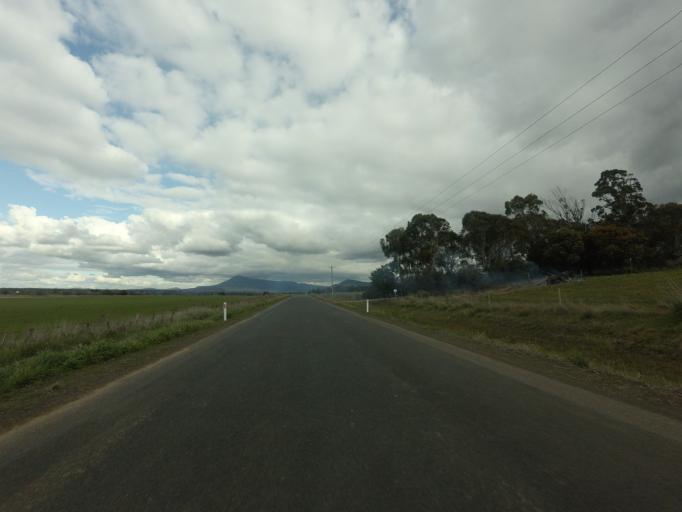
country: AU
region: Tasmania
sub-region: Northern Midlands
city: Longford
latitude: -41.7781
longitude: 147.0962
